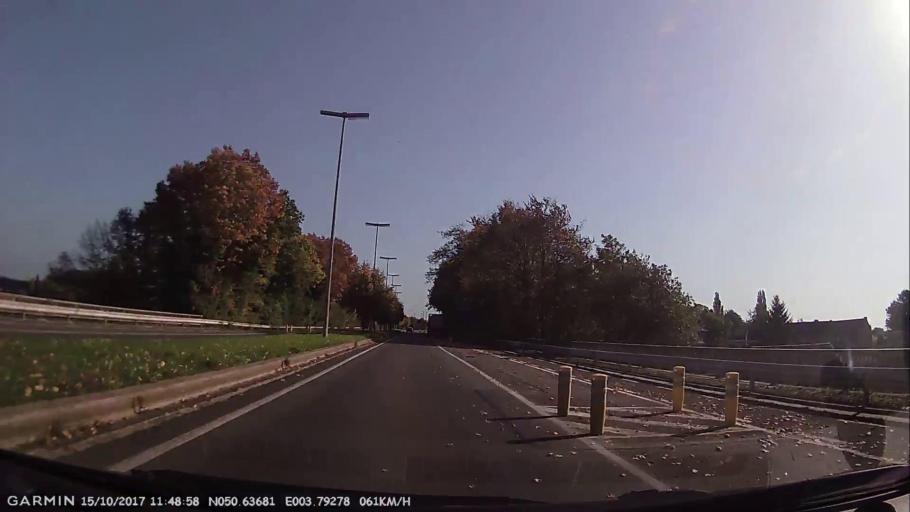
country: BE
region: Wallonia
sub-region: Province du Hainaut
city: Ath
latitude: 50.6368
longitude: 3.7929
